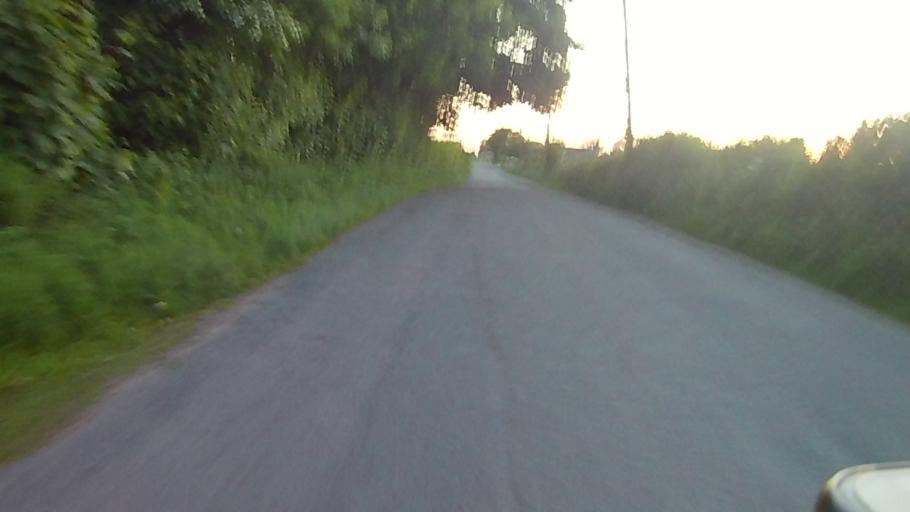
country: IE
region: Munster
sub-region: County Cork
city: Carrigtwohill
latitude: 51.9715
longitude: -8.2453
